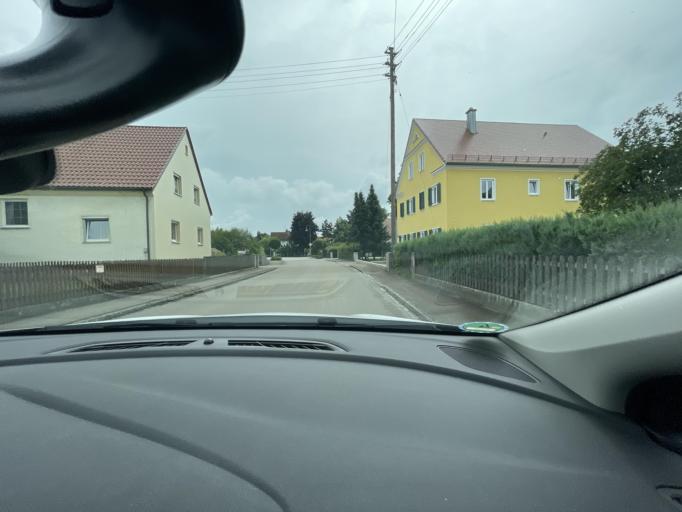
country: DE
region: Bavaria
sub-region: Swabia
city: Westendorf
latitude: 48.5760
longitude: 10.8565
